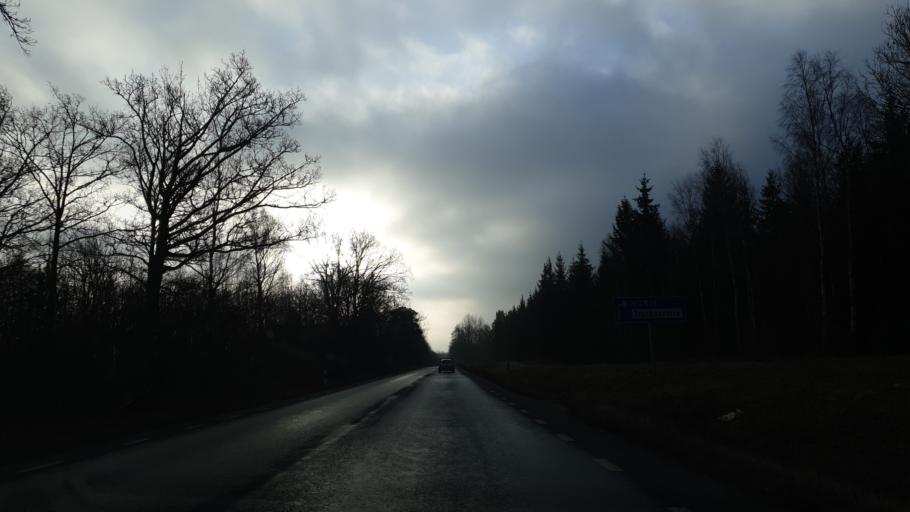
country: SE
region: Blekinge
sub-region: Karlshamns Kommun
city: Morrum
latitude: 56.1415
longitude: 14.6701
